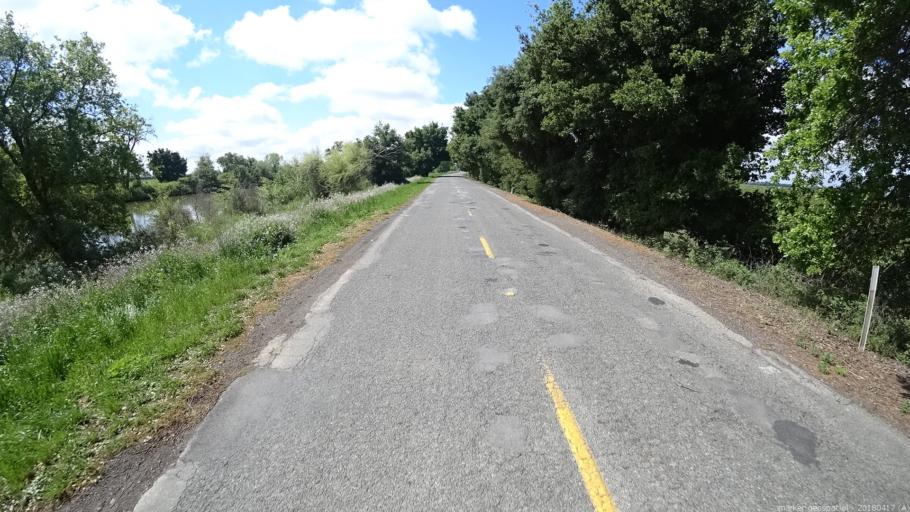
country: US
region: California
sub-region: Sacramento County
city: Walnut Grove
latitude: 38.2327
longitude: -121.5214
